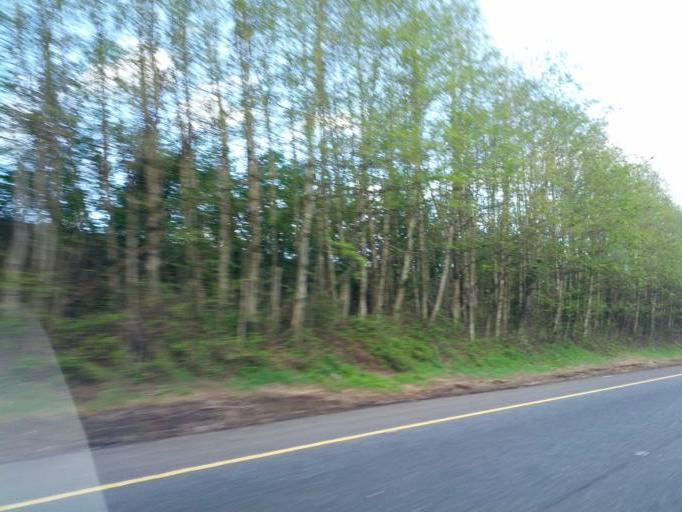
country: IE
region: Leinster
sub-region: Kildare
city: Kilcock
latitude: 53.3924
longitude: -6.6756
